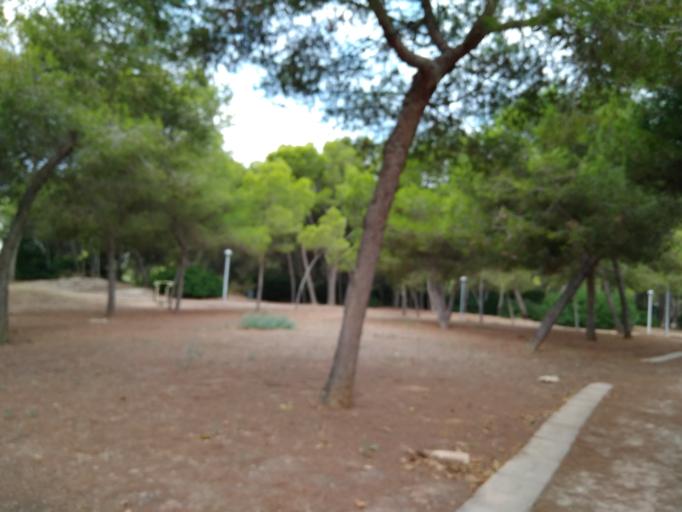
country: ES
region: Balearic Islands
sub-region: Illes Balears
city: s'Arenal
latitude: 39.5280
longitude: 2.7391
